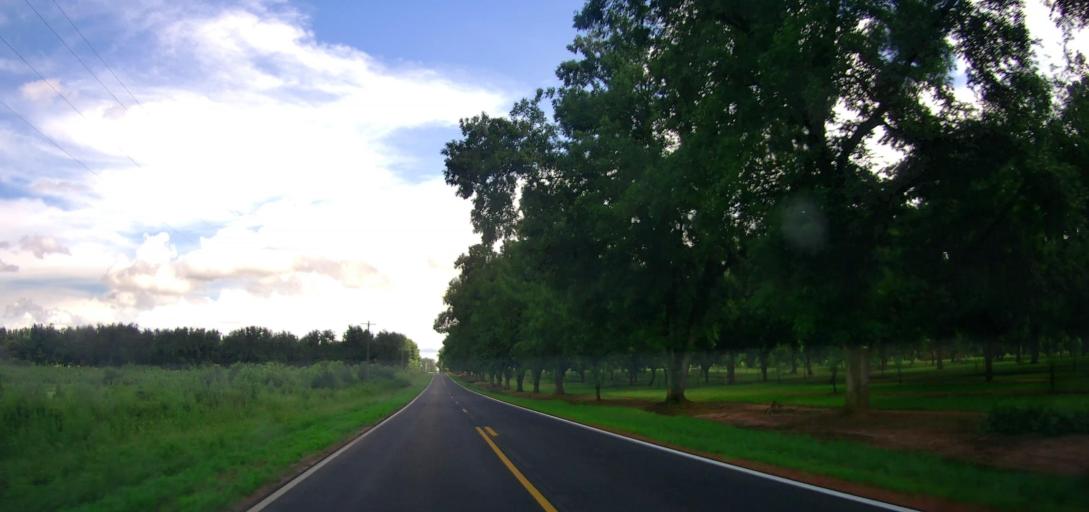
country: US
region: Georgia
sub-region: Macon County
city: Marshallville
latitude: 32.4727
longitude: -83.8900
